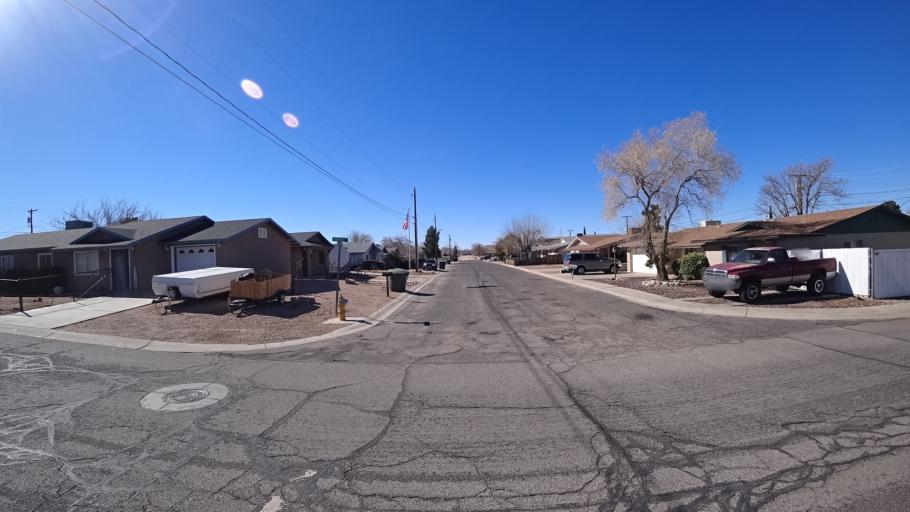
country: US
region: Arizona
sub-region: Mohave County
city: Kingman
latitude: 35.2089
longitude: -114.0212
